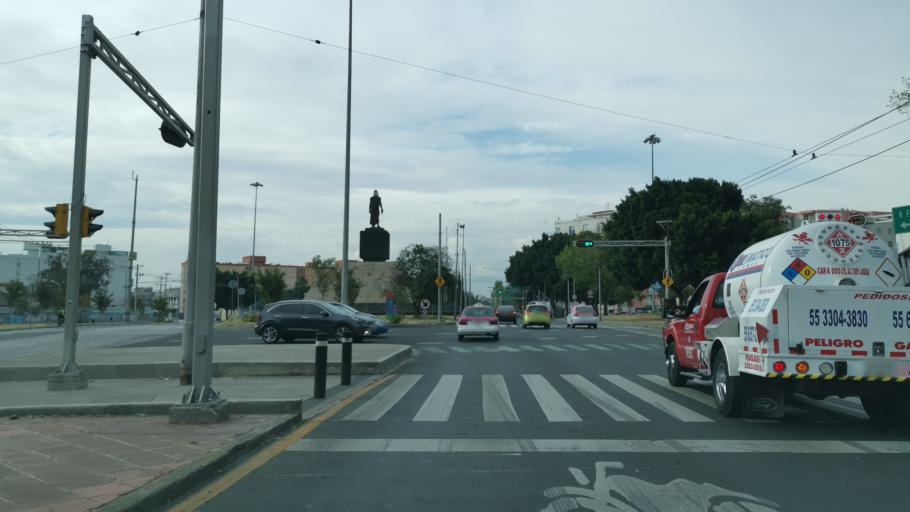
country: MX
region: Mexico City
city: Cuauhtemoc
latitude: 19.4491
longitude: -99.1340
